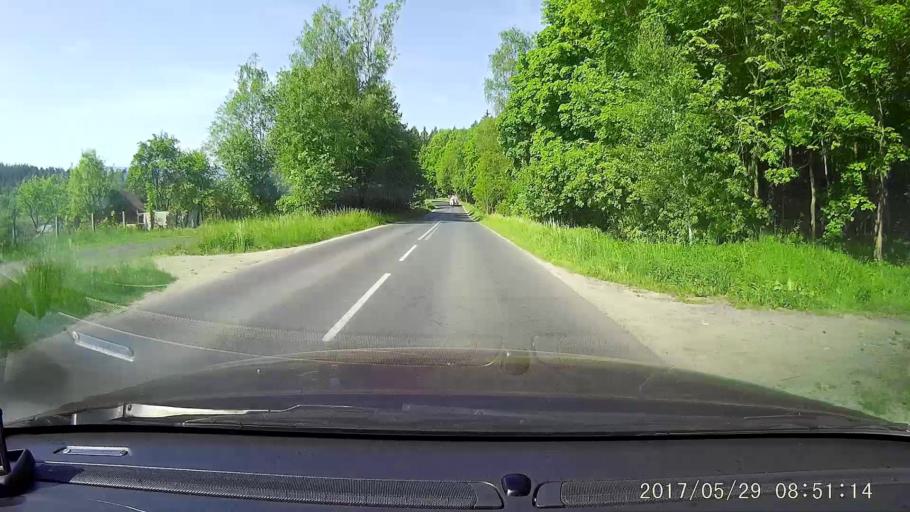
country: PL
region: Lower Silesian Voivodeship
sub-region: Powiat jeleniogorski
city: Jezow Sudecki
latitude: 50.9308
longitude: 15.7752
